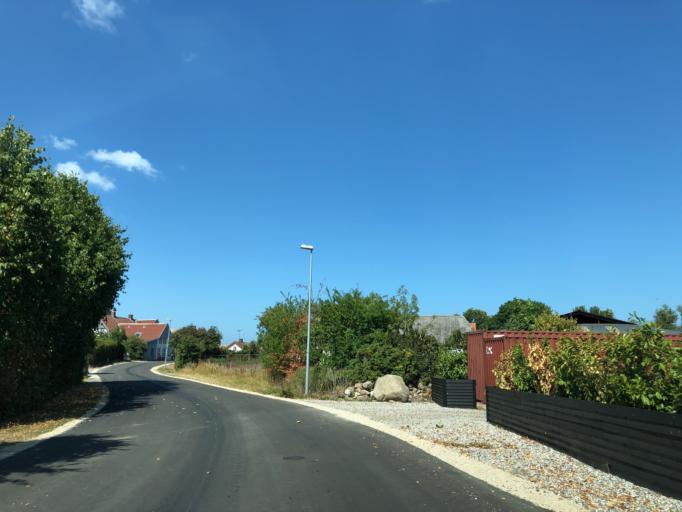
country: DK
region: Capital Region
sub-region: Halsnaes Kommune
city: Liseleje
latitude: 55.9748
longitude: 11.9148
